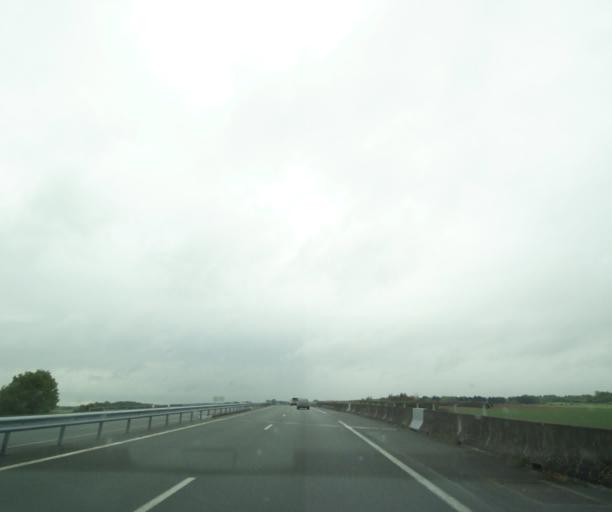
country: FR
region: Poitou-Charentes
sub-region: Departement de la Charente-Maritime
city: Nieul-les-Saintes
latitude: 45.6989
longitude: -0.7481
